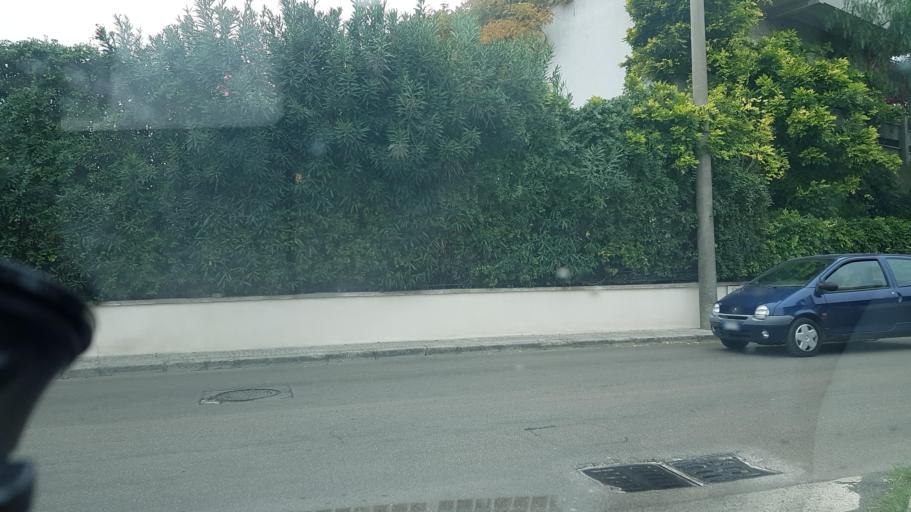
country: IT
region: Apulia
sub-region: Provincia di Lecce
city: Leverano
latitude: 40.2890
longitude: 18.0053
